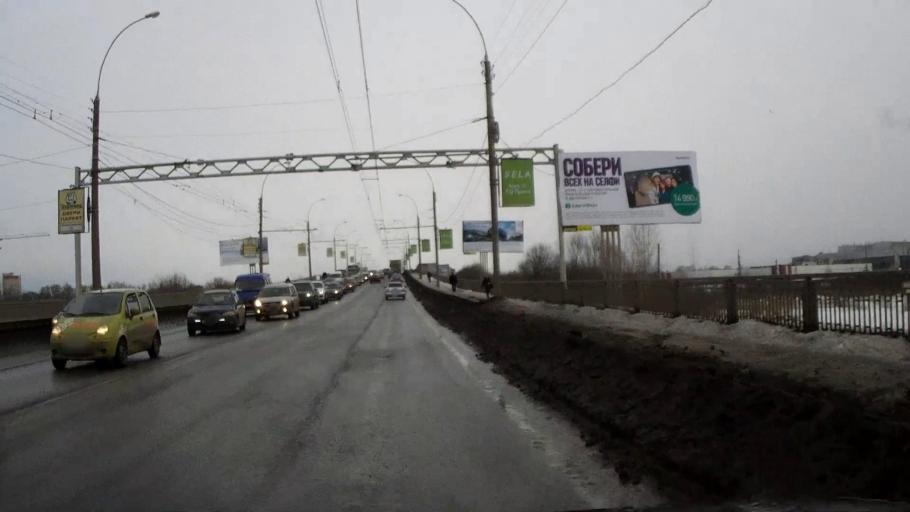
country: RU
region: Vologda
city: Vologda
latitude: 59.2148
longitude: 39.8582
